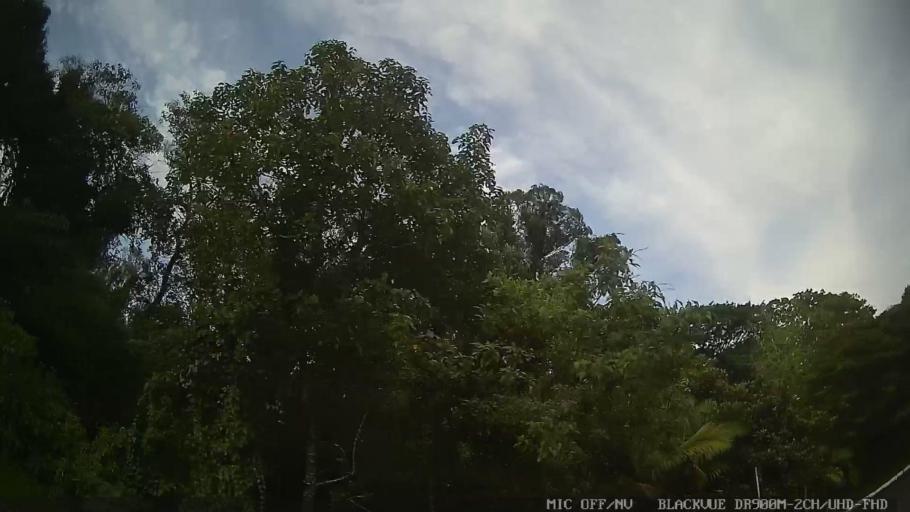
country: BR
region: Sao Paulo
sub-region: Amparo
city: Amparo
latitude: -22.6878
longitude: -46.7334
